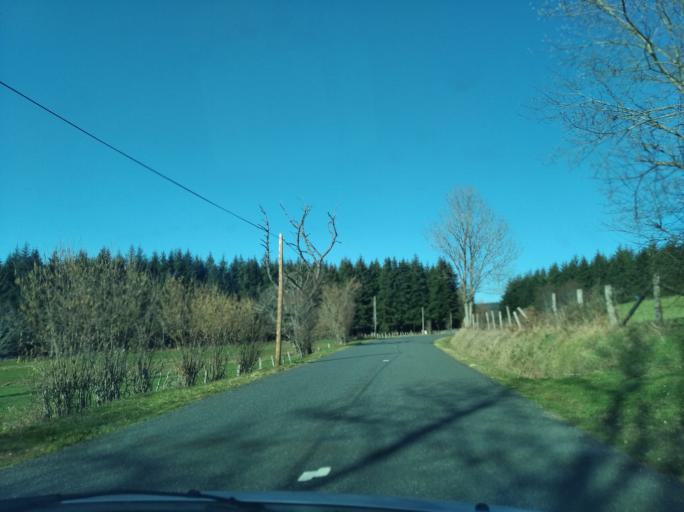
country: FR
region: Rhone-Alpes
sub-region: Departement de la Loire
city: Ambierle
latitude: 46.1079
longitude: 3.7865
